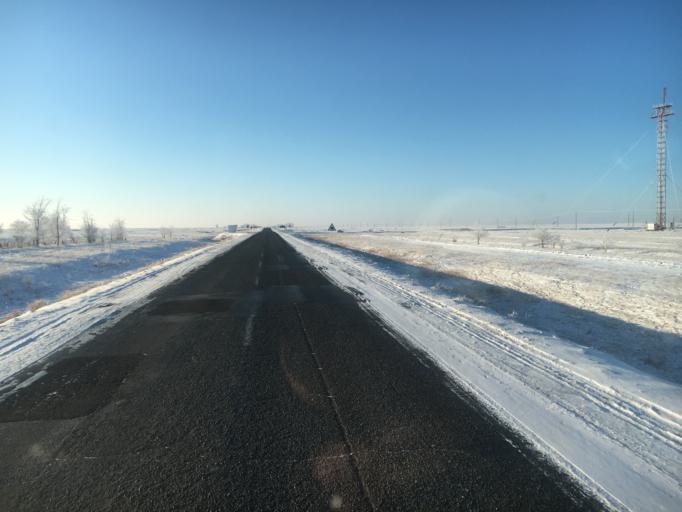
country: RU
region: Orenburg
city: Dombarovskiy
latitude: 50.1104
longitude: 59.3046
